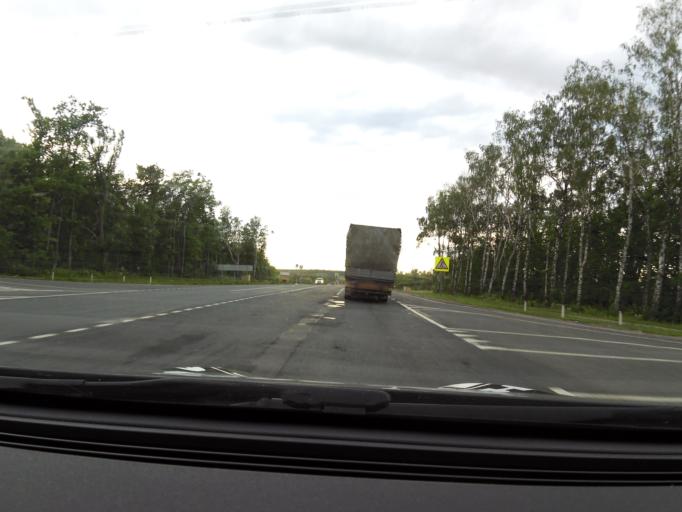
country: RU
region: Chuvashia
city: Tsivil'sk
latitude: 55.9223
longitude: 47.4035
